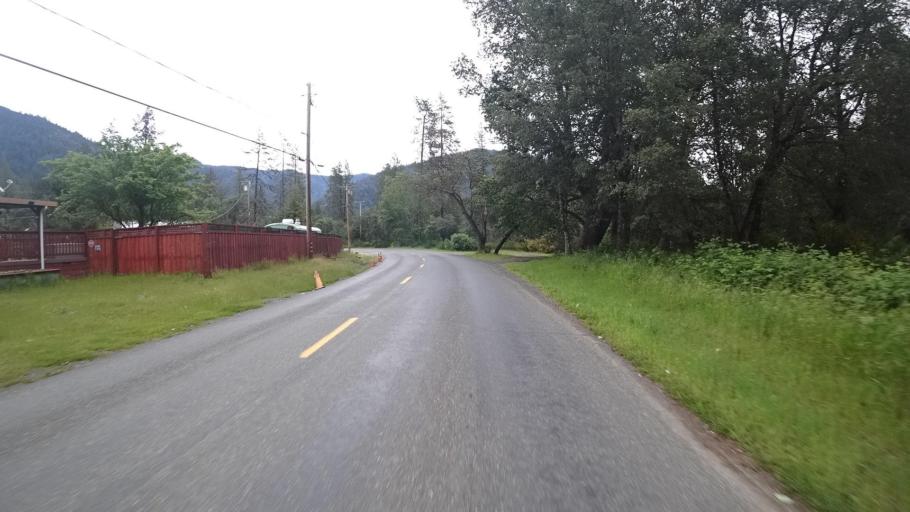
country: US
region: California
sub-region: Humboldt County
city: Willow Creek
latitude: 40.9474
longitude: -123.6293
